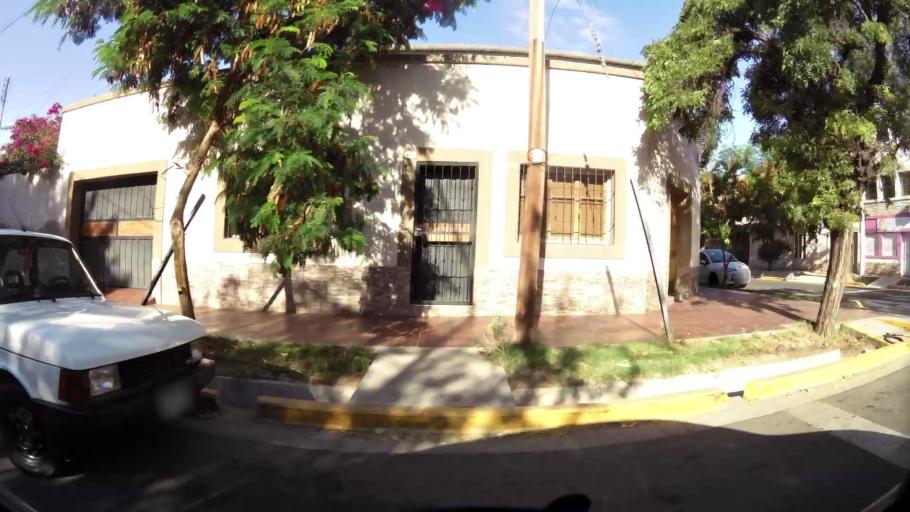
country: AR
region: Mendoza
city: Mendoza
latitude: -32.9007
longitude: -68.8351
